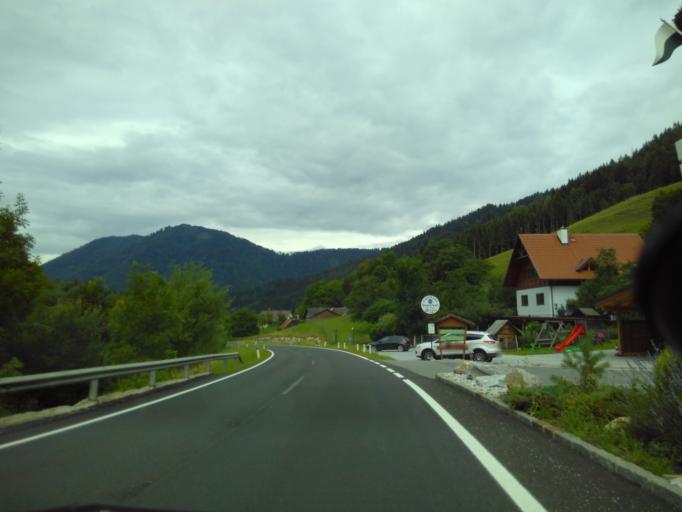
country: AT
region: Styria
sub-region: Politischer Bezirk Graz-Umgebung
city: Schrems bei Frohnleiten
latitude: 47.2755
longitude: 15.3831
